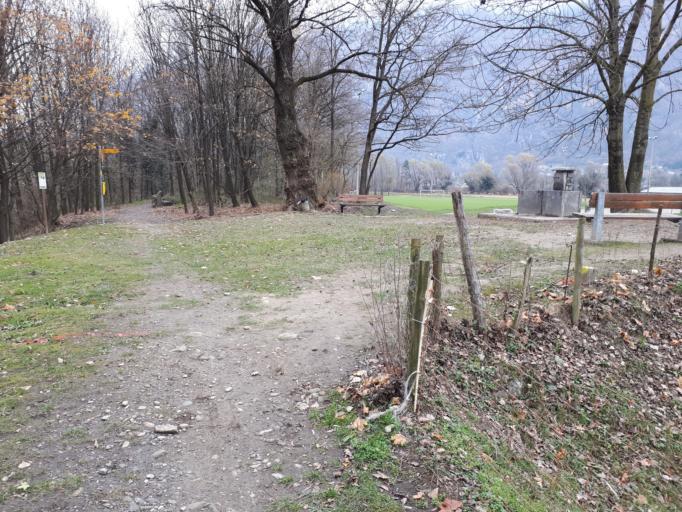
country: CH
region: Ticino
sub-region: Riviera District
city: Claro
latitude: 46.2557
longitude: 9.0112
